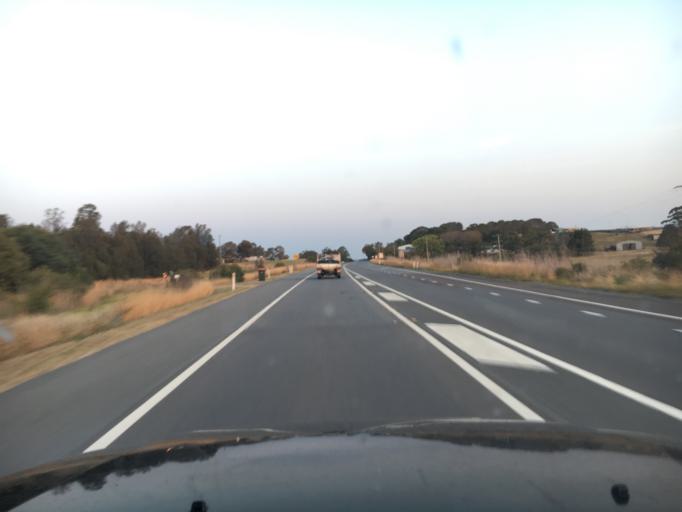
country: AU
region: New South Wales
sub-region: Cessnock
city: Greta
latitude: -32.7007
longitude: 151.4128
